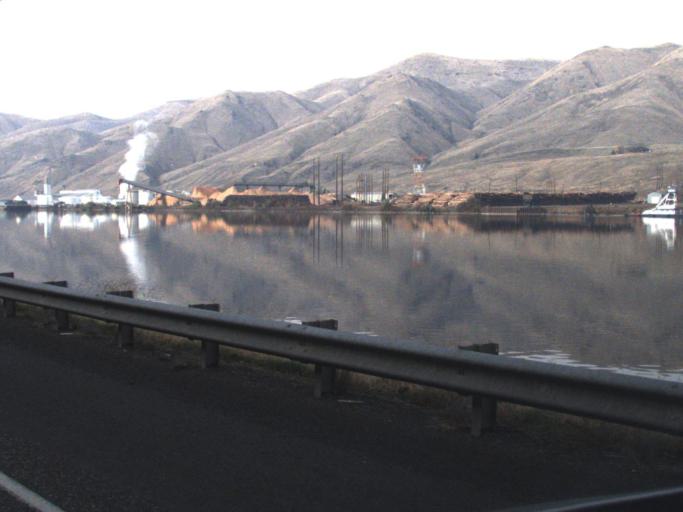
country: US
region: Washington
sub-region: Asotin County
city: Clarkston Heights-Vineland
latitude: 46.4166
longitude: -117.1011
